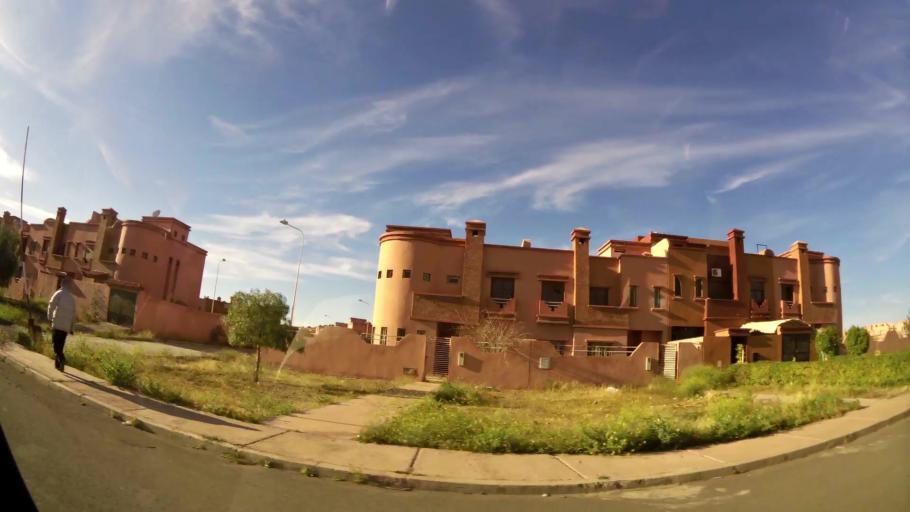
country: MA
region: Marrakech-Tensift-Al Haouz
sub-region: Marrakech
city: Marrakesh
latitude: 31.7556
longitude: -8.1043
